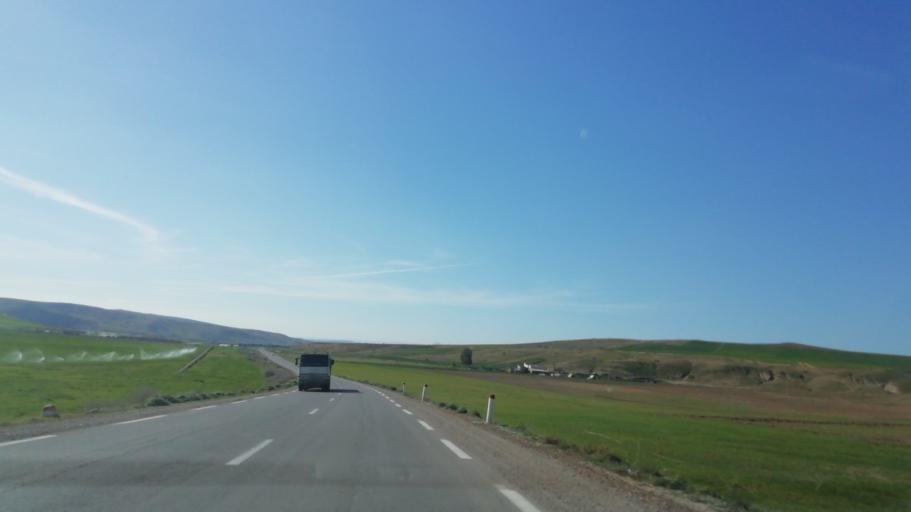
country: DZ
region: Mascara
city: Oued el Abtal
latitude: 35.4497
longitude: 0.8051
